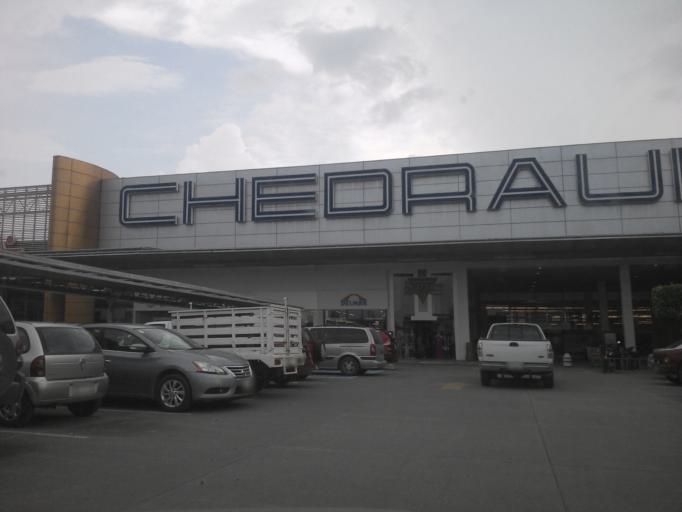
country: MX
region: Veracruz
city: Martinez de la Torre
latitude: 20.0707
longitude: -97.0641
